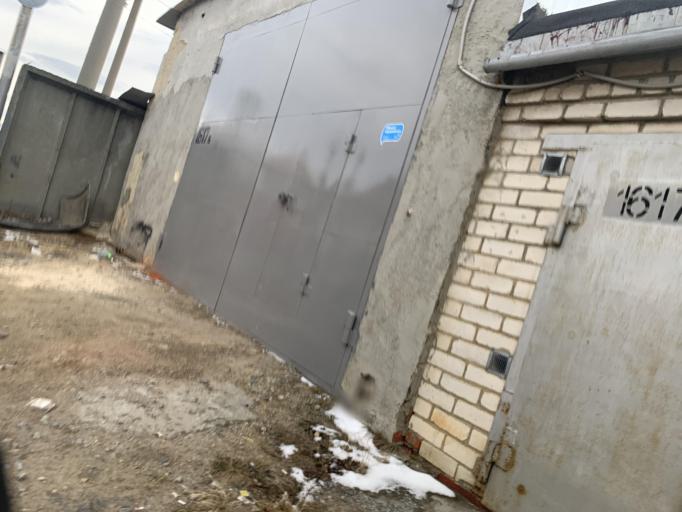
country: RU
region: Chelyabinsk
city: Roshchino
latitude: 55.1875
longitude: 61.2686
